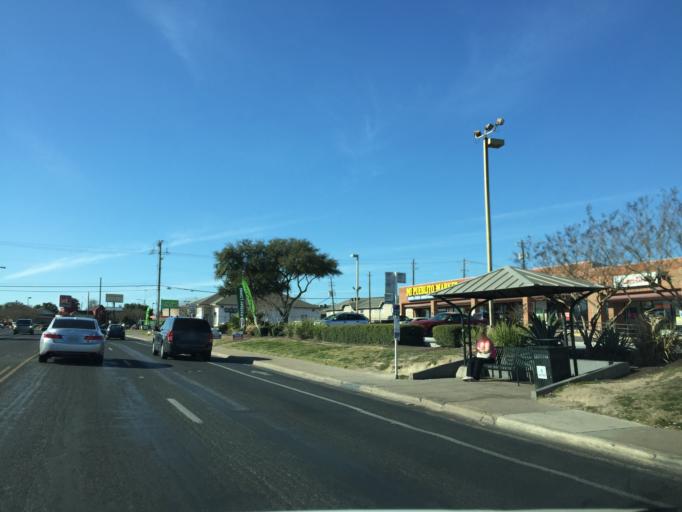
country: US
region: Texas
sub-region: Travis County
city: Austin
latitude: 30.2304
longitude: -97.7322
